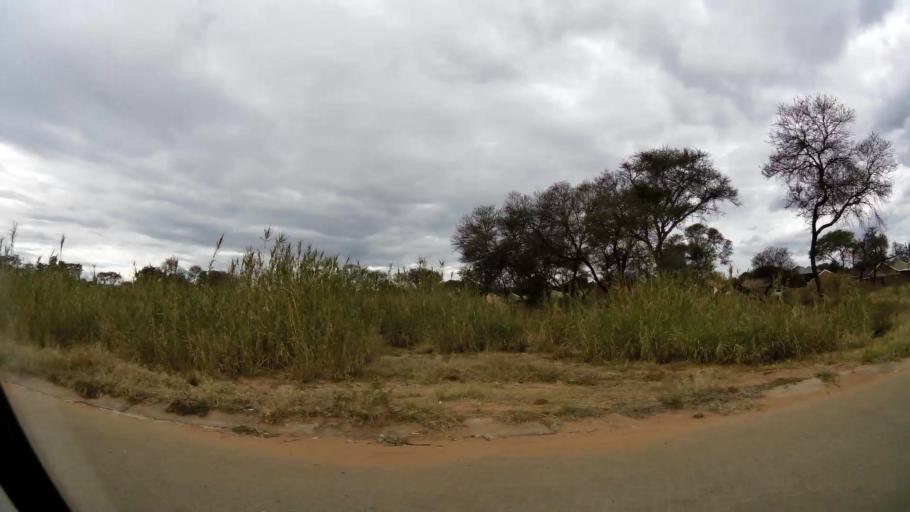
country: ZA
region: Limpopo
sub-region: Waterberg District Municipality
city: Modimolle
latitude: -24.7010
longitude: 28.4185
